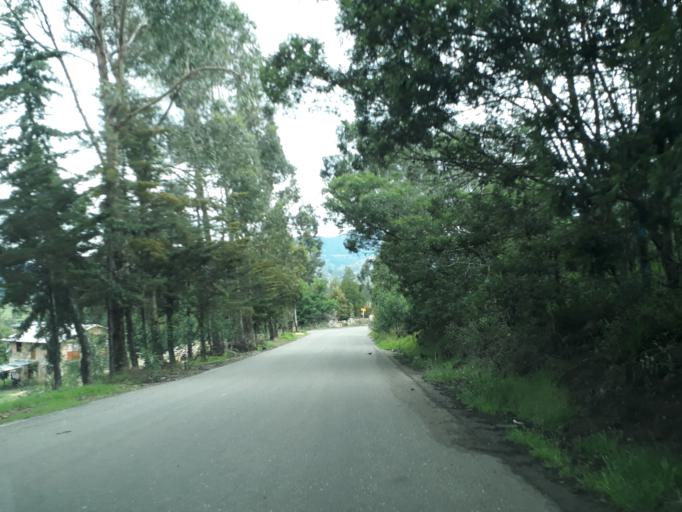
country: CO
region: Cundinamarca
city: Cucunuba
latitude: 5.2362
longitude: -73.7761
